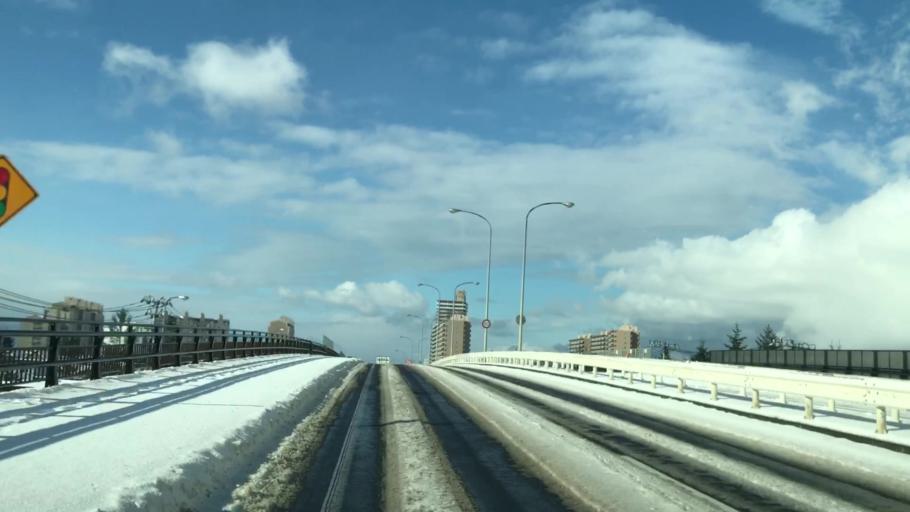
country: JP
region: Hokkaido
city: Ishikari
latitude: 43.1572
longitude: 141.4096
